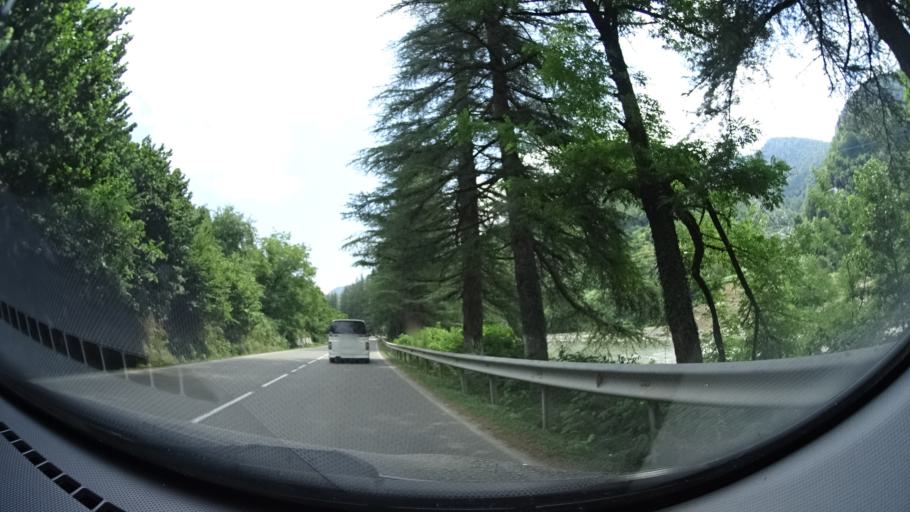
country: TR
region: Artvin
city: Camili
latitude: 41.5667
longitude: 41.8391
